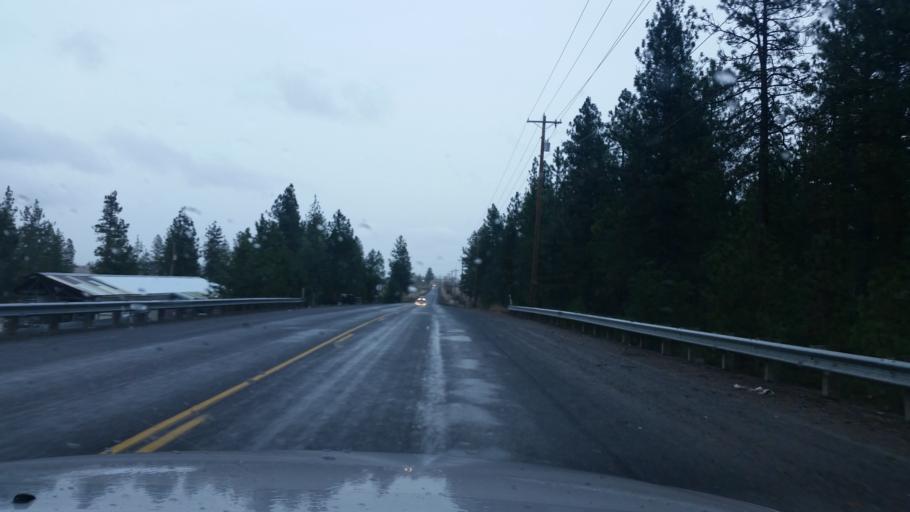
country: US
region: Washington
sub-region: Spokane County
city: Airway Heights
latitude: 47.6719
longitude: -117.5850
